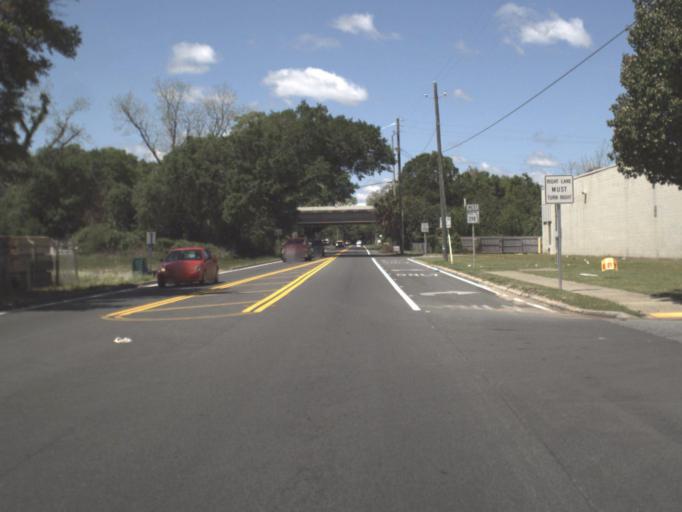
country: US
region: Florida
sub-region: Escambia County
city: West Pensacola
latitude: 30.4263
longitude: -87.2726
